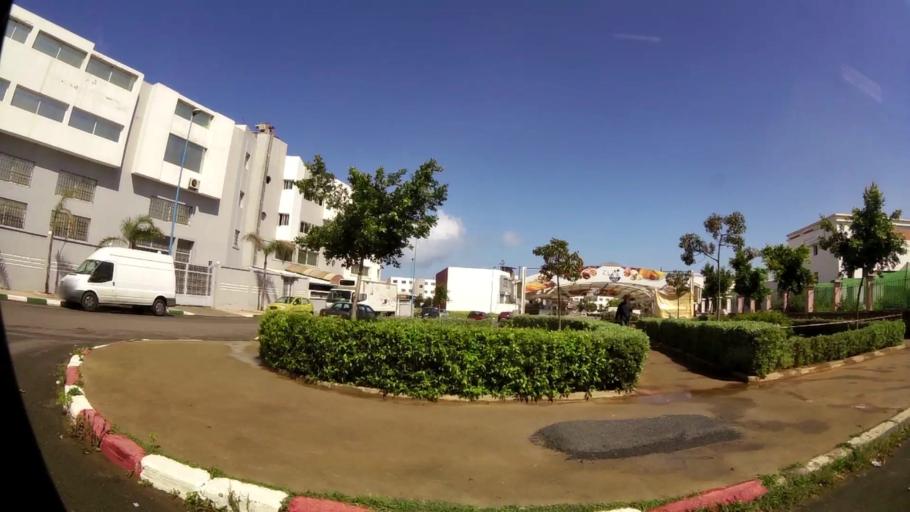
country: MA
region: Grand Casablanca
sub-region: Mediouna
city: Tit Mellil
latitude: 33.6198
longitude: -7.5060
